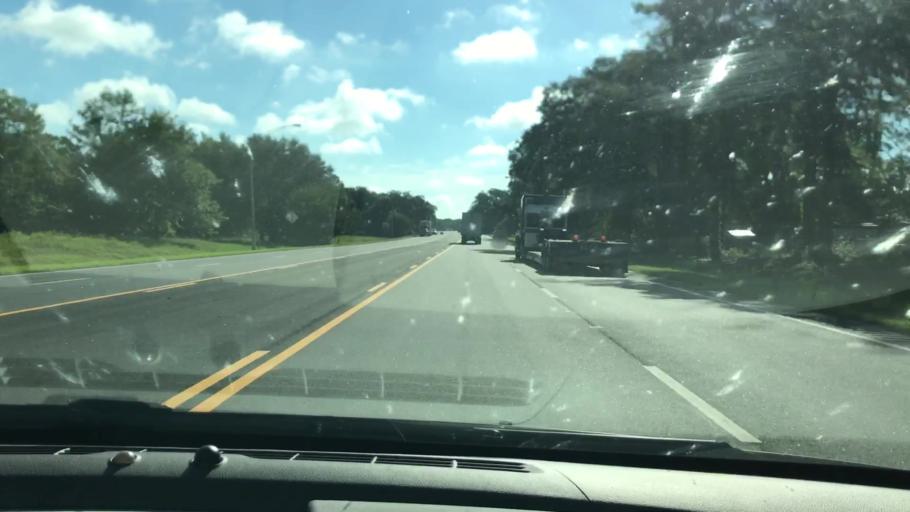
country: US
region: Georgia
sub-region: Dougherty County
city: Albany
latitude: 31.5801
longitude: -84.0825
